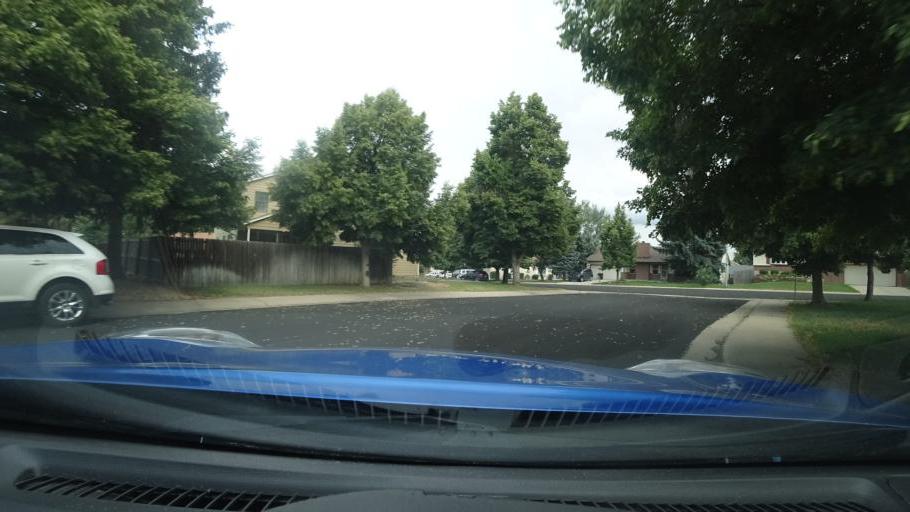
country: US
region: Colorado
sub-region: Adams County
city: Aurora
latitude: 39.6919
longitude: -104.8122
